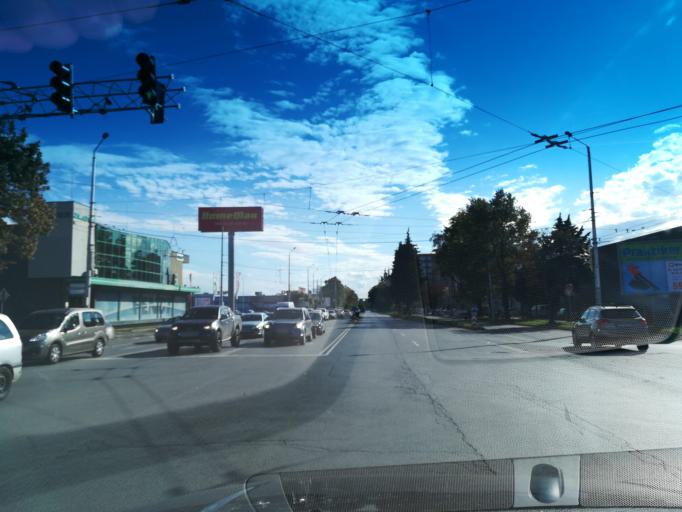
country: BG
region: Stara Zagora
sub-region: Obshtina Stara Zagora
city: Stara Zagora
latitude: 42.4149
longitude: 25.6383
